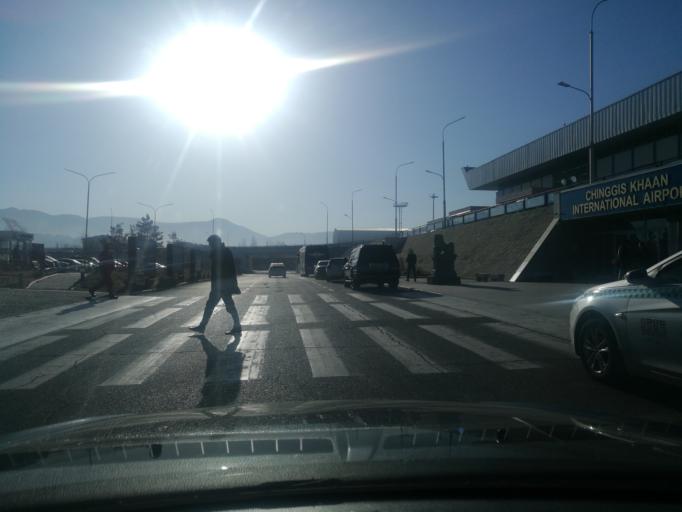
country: MN
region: Ulaanbaatar
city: Ulaanbaatar
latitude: 47.8530
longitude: 106.7631
